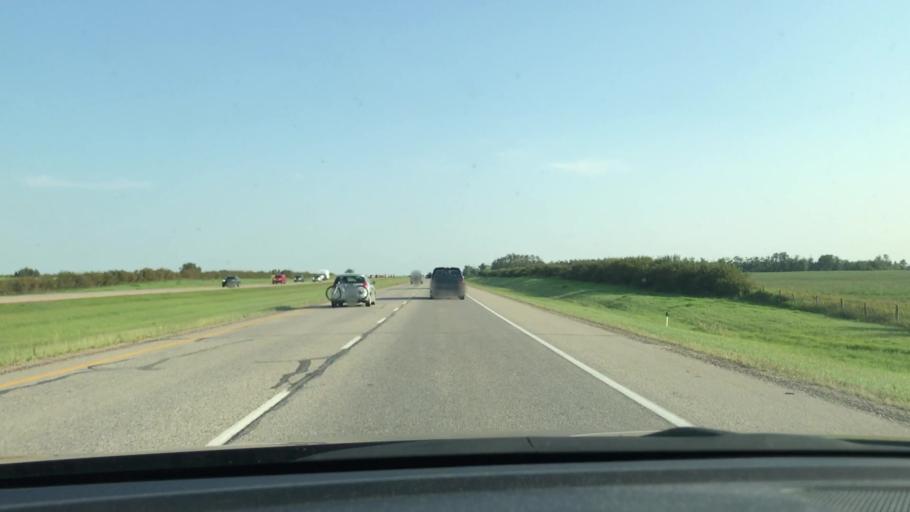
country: CA
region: Alberta
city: Millet
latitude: 53.0761
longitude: -113.5986
